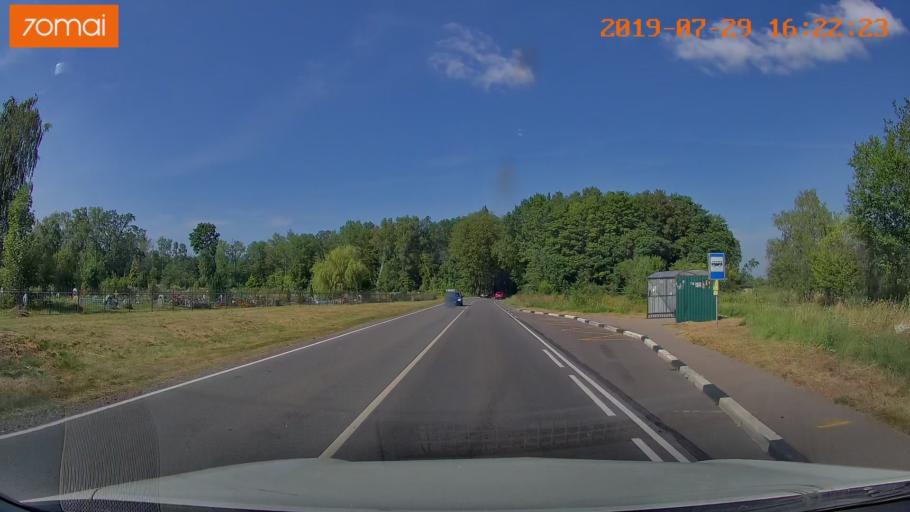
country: RU
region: Kaliningrad
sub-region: Gorod Kaliningrad
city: Baltiysk
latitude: 54.6976
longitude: 19.9386
